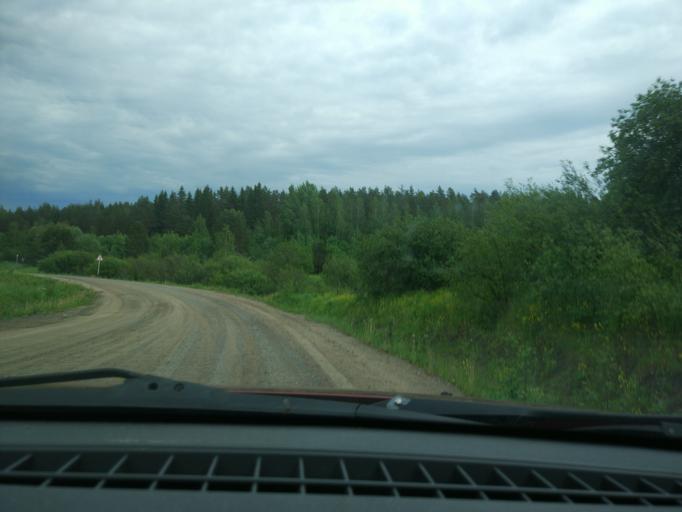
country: RU
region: Leningrad
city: Kuznechnoye
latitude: 61.2817
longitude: 29.8559
